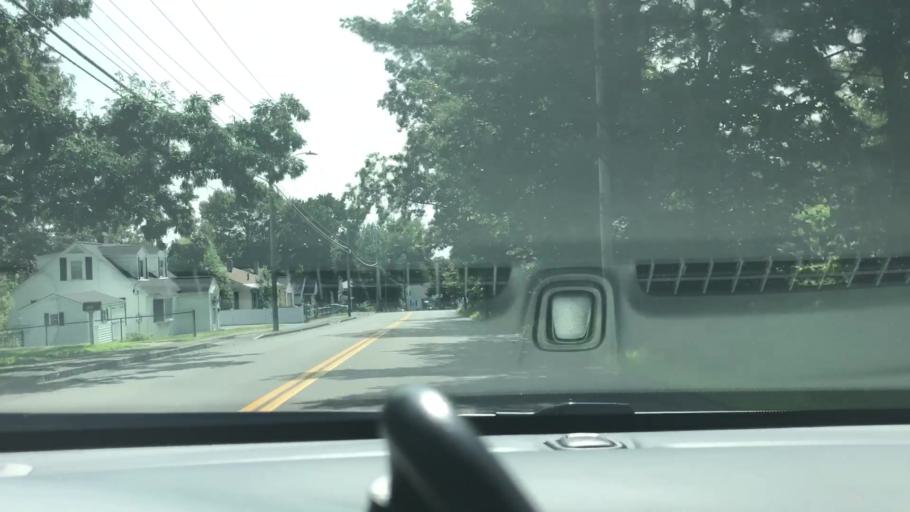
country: US
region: New Hampshire
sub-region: Hillsborough County
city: Pinardville
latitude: 42.9846
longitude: -71.4903
